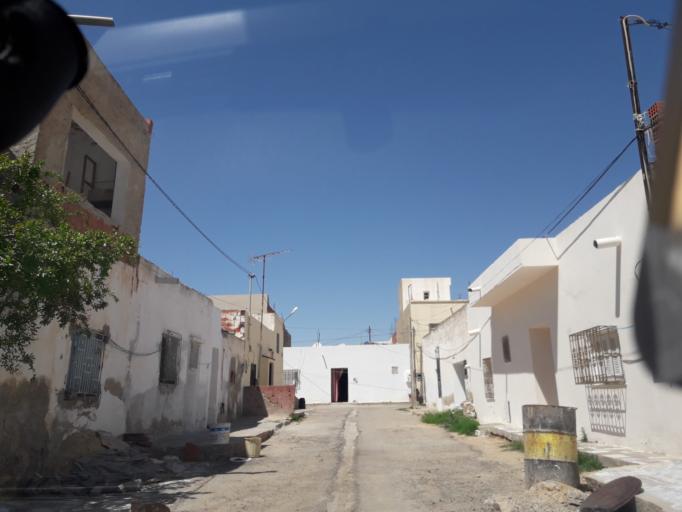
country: TN
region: Safaqis
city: Sfax
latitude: 34.7387
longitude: 10.5225
